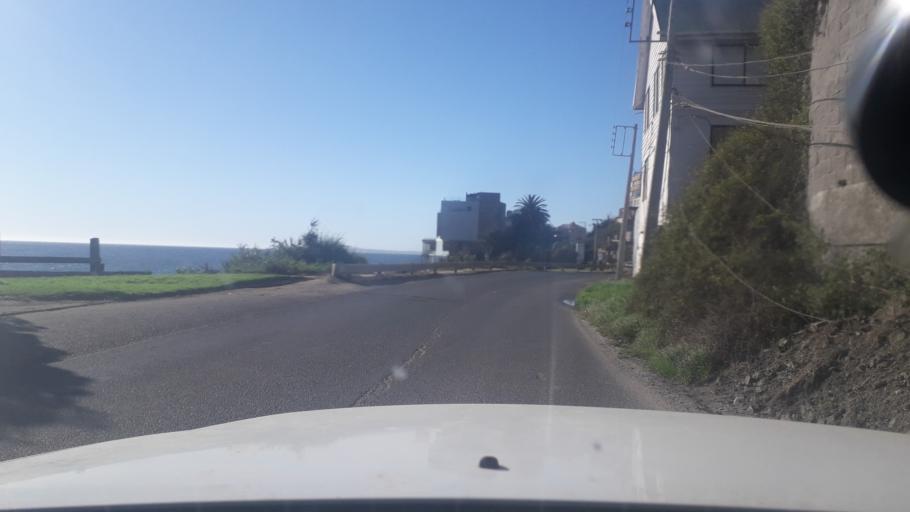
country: CL
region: Valparaiso
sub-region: Provincia de Valparaiso
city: Vina del Mar
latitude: -32.9205
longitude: -71.5237
